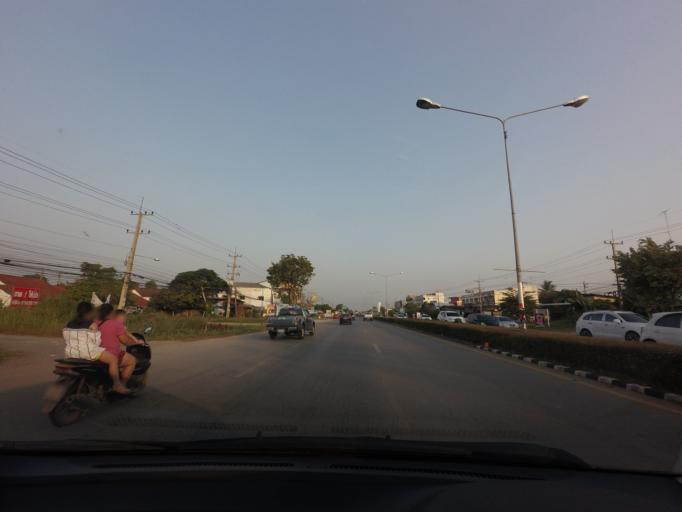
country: TH
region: Sukhothai
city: Sukhothai
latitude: 17.0220
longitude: 99.8170
